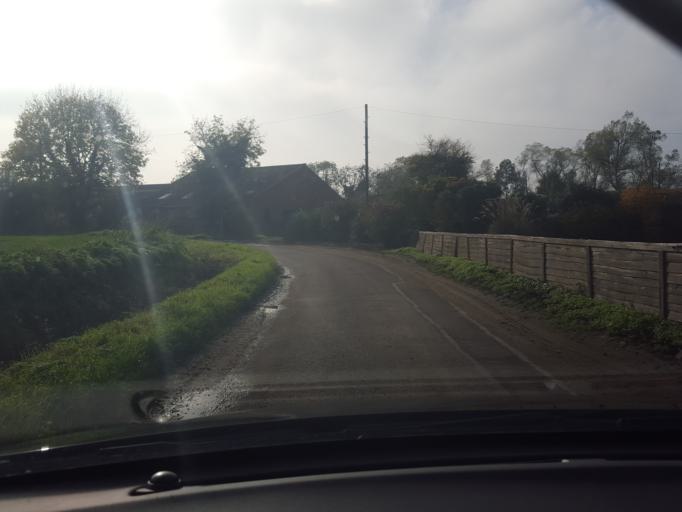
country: GB
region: England
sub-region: Essex
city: Mistley
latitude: 51.9214
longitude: 1.1474
